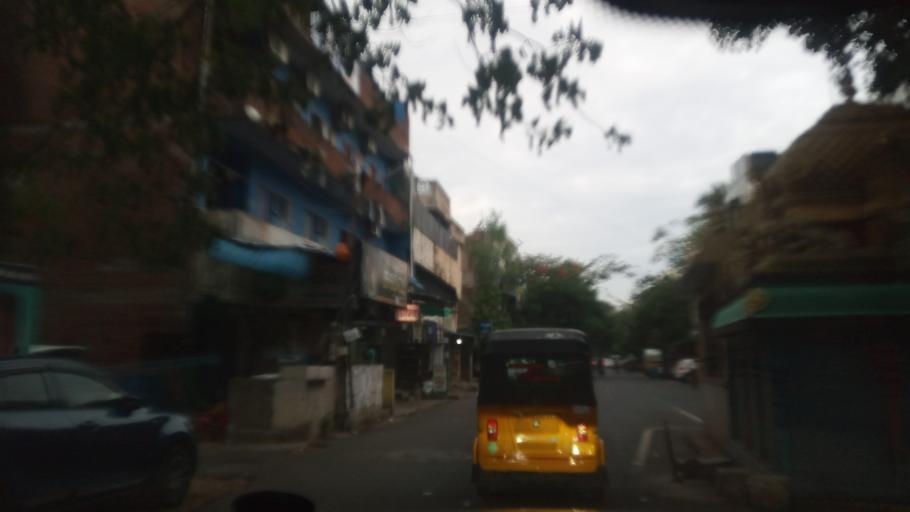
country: IN
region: Tamil Nadu
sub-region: Chennai
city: Chetput
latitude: 13.0419
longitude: 80.2133
